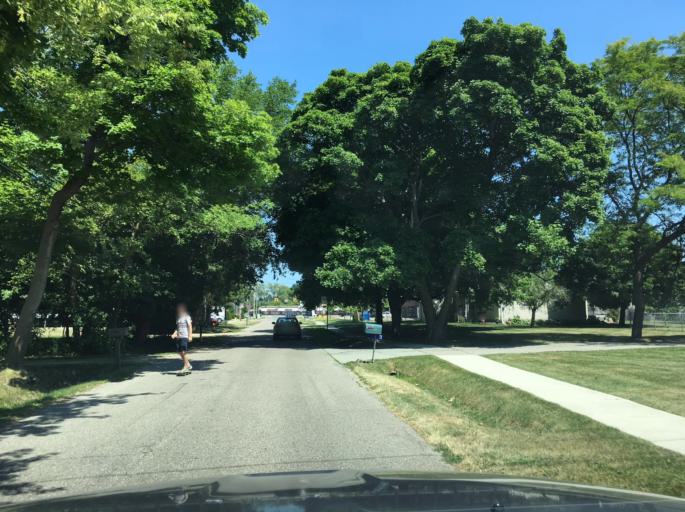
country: US
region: Michigan
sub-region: Macomb County
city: Clinton
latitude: 42.5630
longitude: -82.8978
